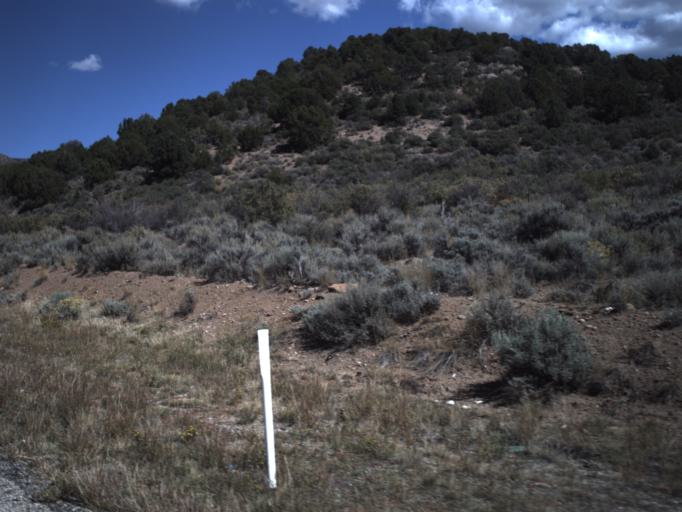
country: US
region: Utah
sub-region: Washington County
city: Enterprise
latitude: 37.4499
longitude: -113.6225
